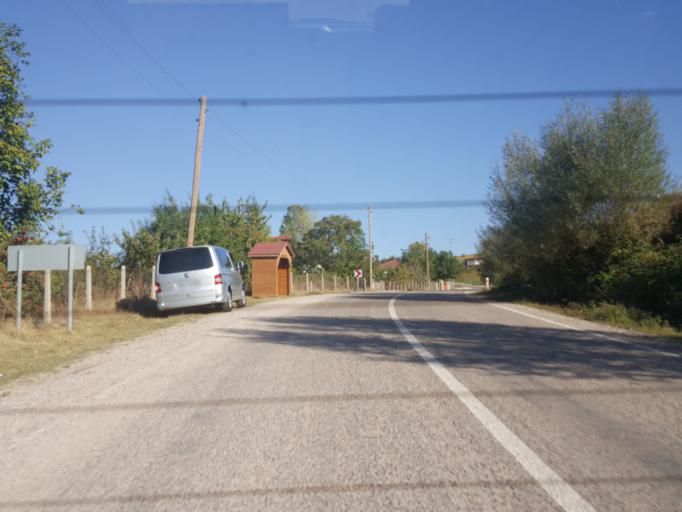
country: TR
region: Amasya
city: Tasova
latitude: 40.7142
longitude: 36.3235
